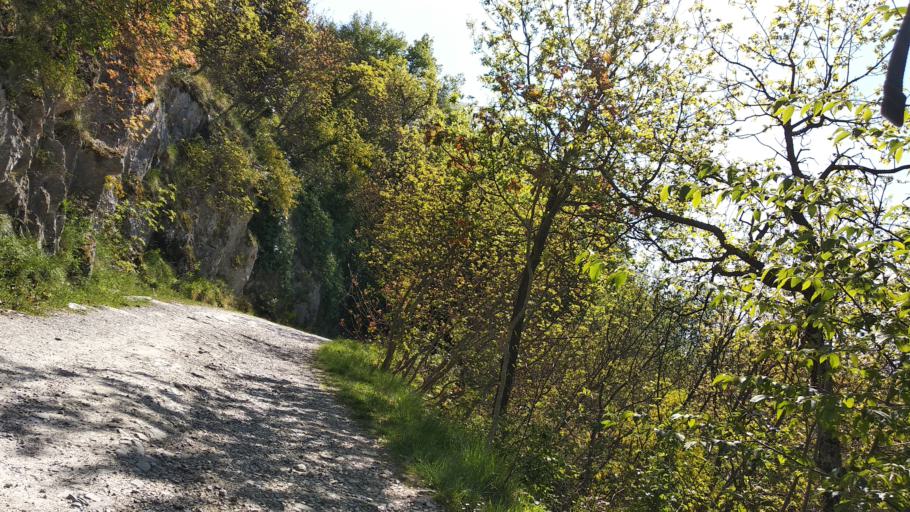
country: IT
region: Emilia-Romagna
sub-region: Provincia di Ravenna
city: Riolo Terme
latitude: 44.2363
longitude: 11.6999
